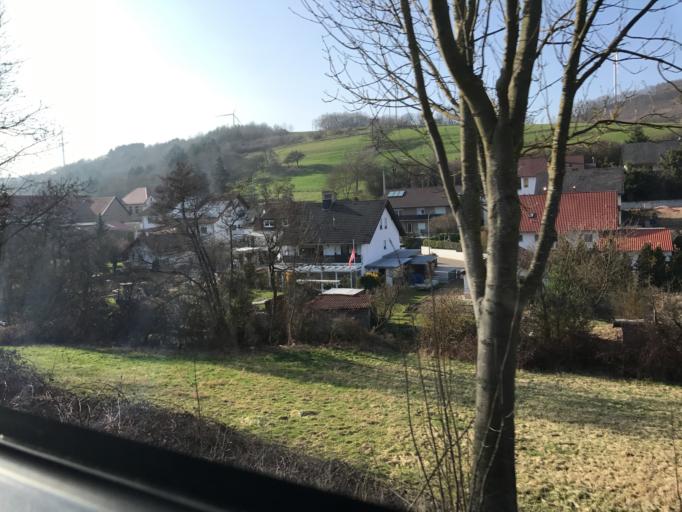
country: DE
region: Rheinland-Pfalz
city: Unkenbach
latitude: 49.7182
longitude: 7.7486
